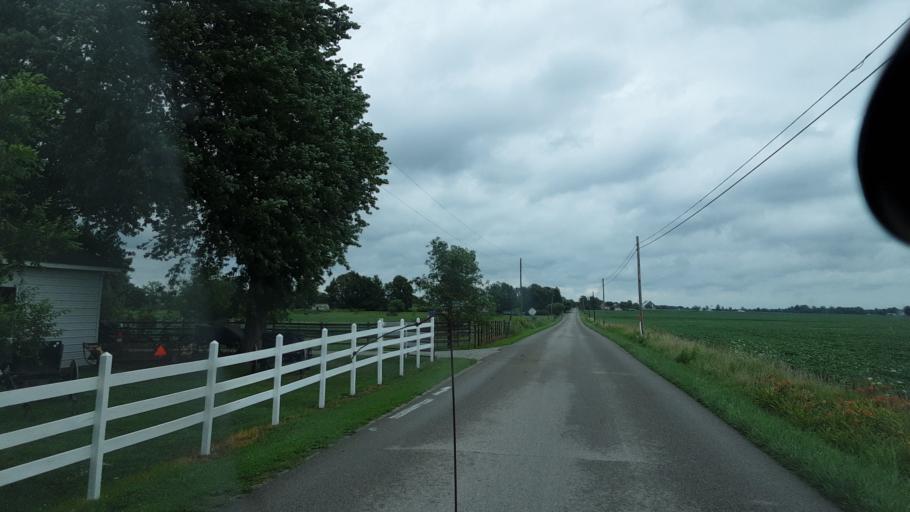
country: US
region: Indiana
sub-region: Adams County
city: Geneva
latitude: 40.5335
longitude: -84.9897
